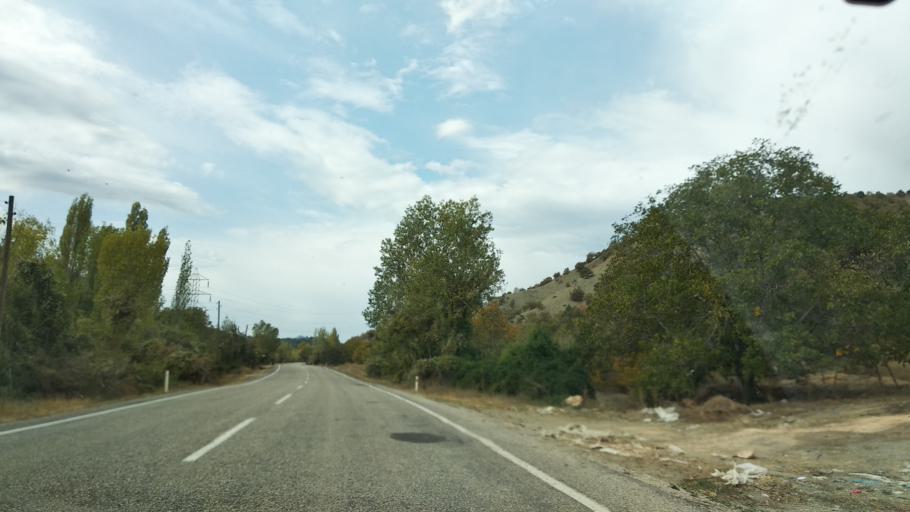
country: TR
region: Ankara
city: Nallihan
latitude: 40.3082
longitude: 31.2849
